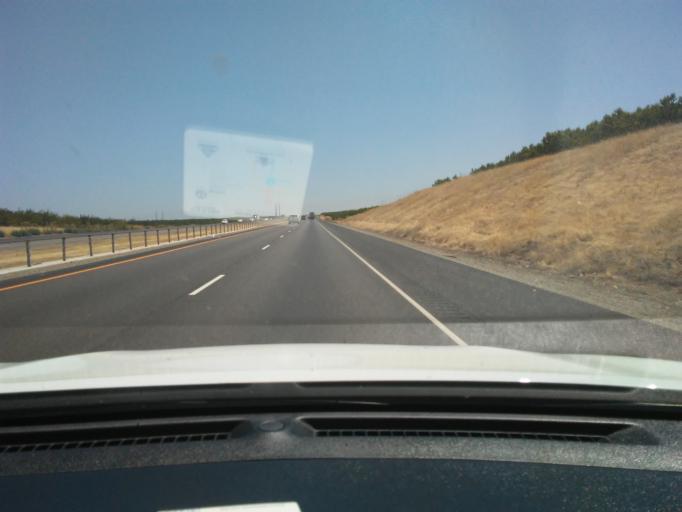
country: US
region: California
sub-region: Stanislaus County
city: Patterson
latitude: 37.5219
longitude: -121.2458
